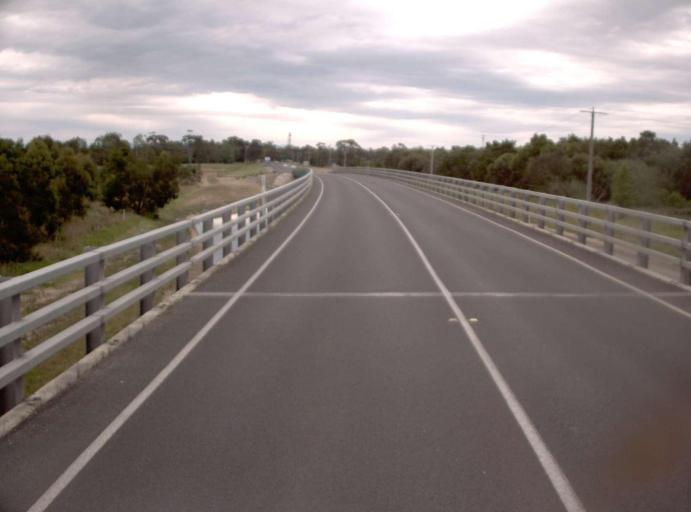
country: AU
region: Victoria
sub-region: Wellington
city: Sale
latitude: -38.1256
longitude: 147.0701
